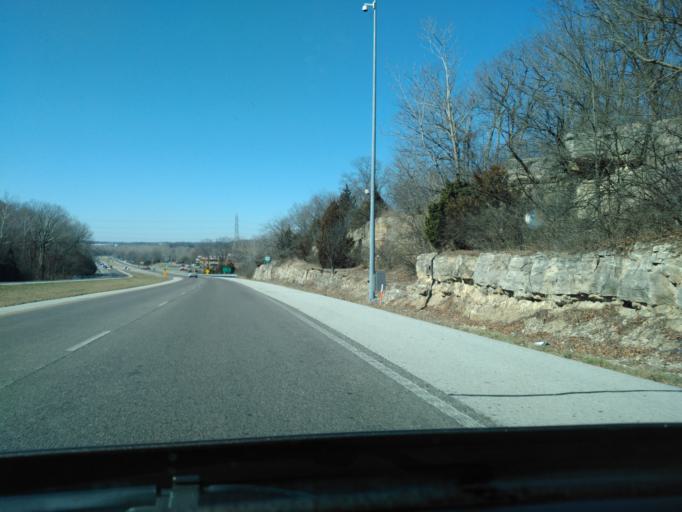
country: US
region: Missouri
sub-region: Saint Louis County
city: Sunset Hills
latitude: 38.5226
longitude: -90.4114
